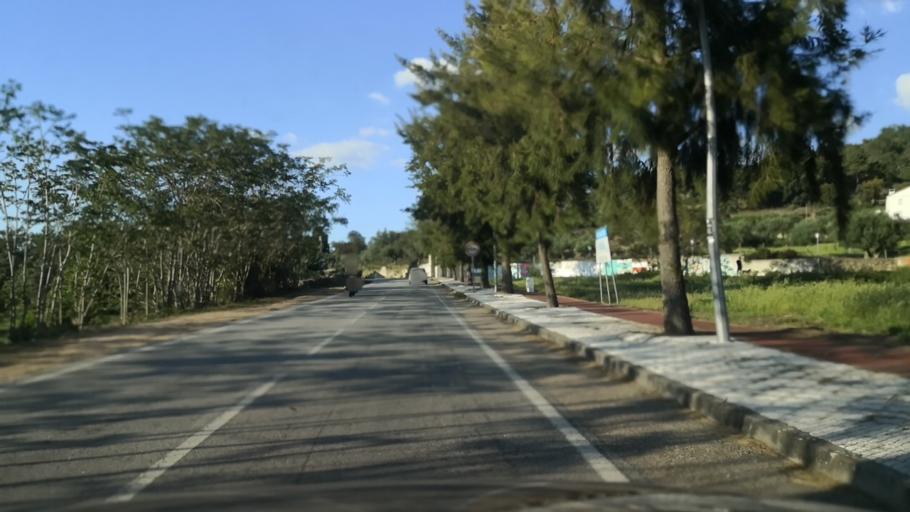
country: PT
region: Portalegre
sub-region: Portalegre
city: Portalegre
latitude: 39.3146
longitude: -7.4405
